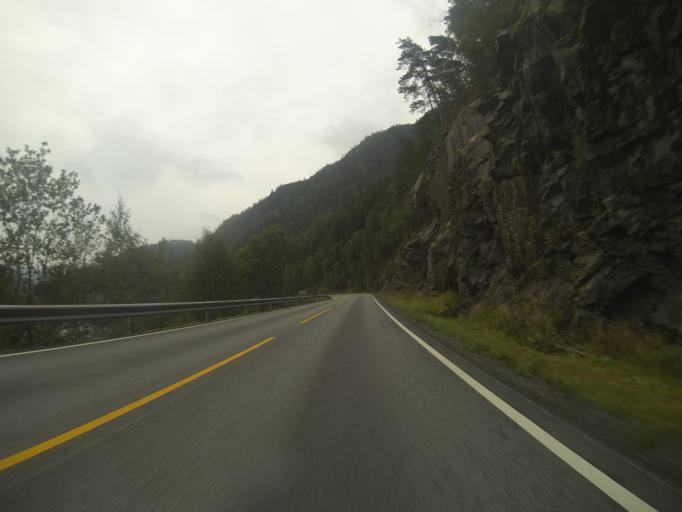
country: NO
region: Rogaland
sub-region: Suldal
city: Sand
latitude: 59.4733
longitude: 6.1924
